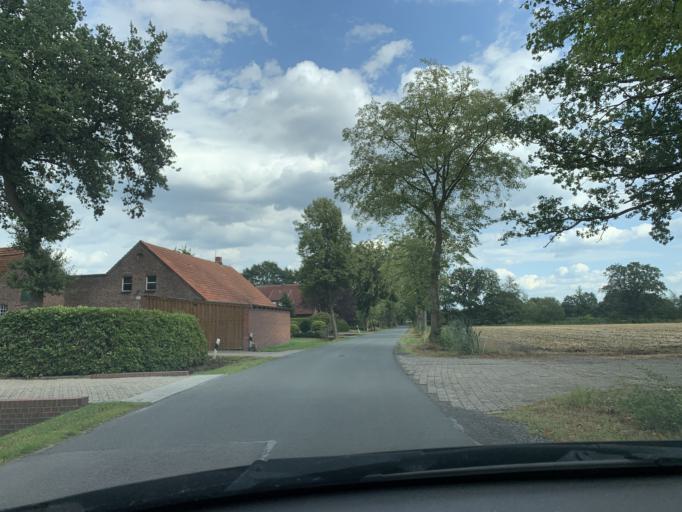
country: DE
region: Lower Saxony
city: Westerstede
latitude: 53.2559
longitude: 7.8772
